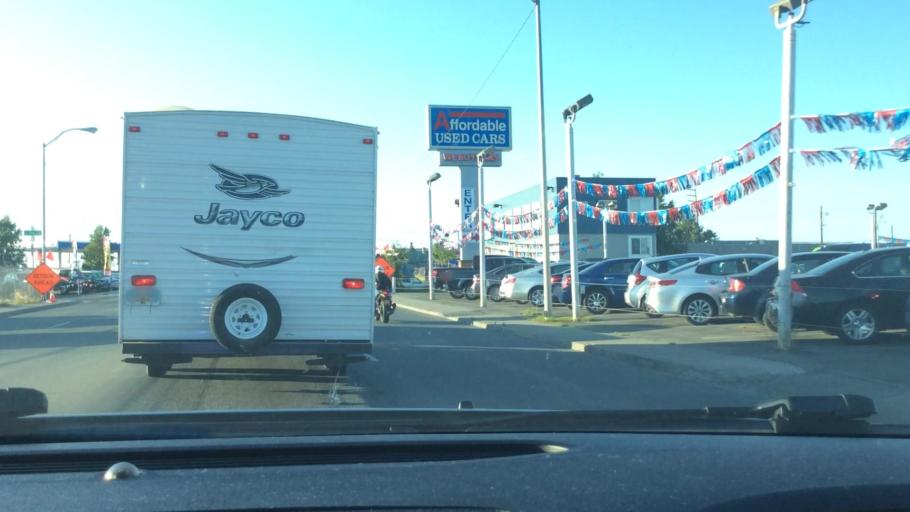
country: US
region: Alaska
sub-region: Anchorage Municipality
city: Anchorage
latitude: 61.2150
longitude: -149.8669
